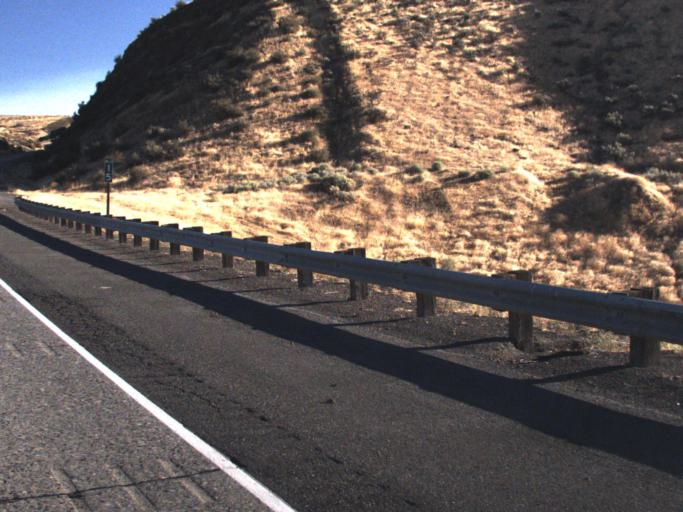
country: US
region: Washington
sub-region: Kittitas County
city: Kittitas
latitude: 46.8006
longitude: -120.3589
